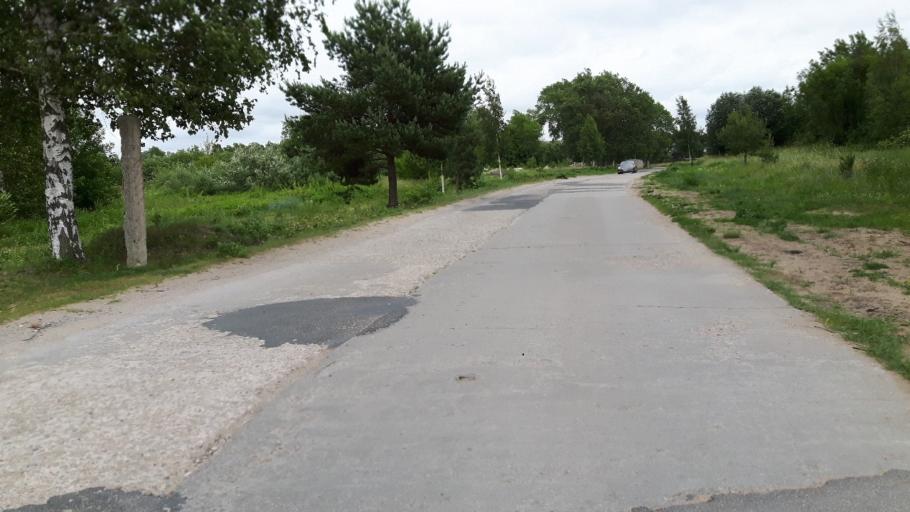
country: LV
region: Liepaja
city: Vec-Liepaja
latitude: 56.5575
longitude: 21.0016
